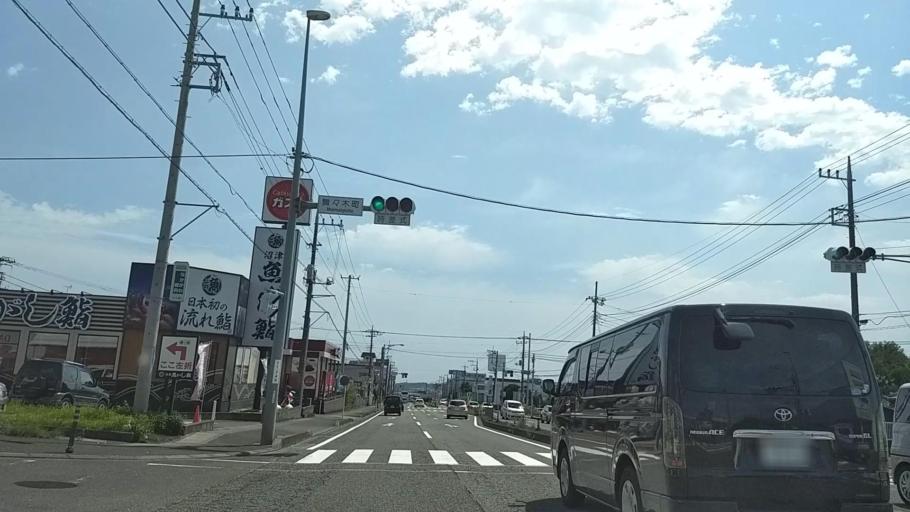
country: JP
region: Shizuoka
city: Fujinomiya
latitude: 35.2372
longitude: 138.6201
